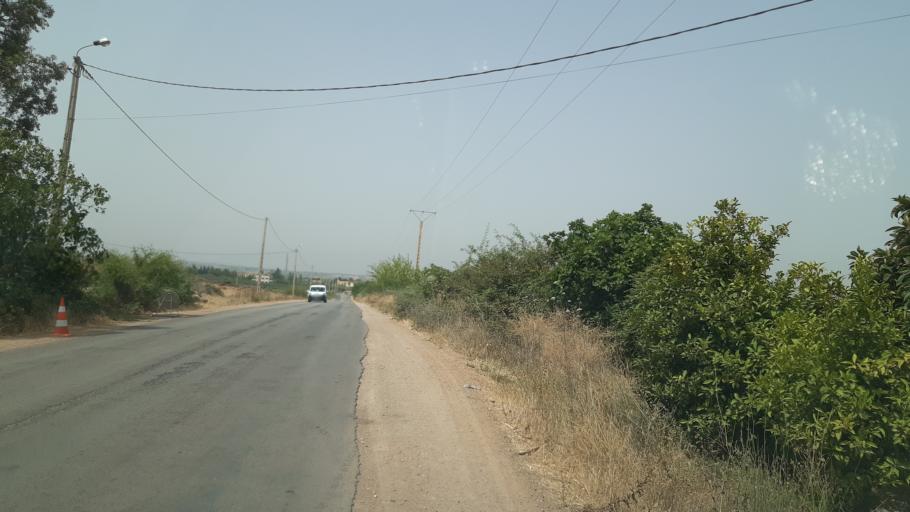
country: MA
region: Fes-Boulemane
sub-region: Fes
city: Oulad Tayeb
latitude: 33.8349
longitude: -5.1438
